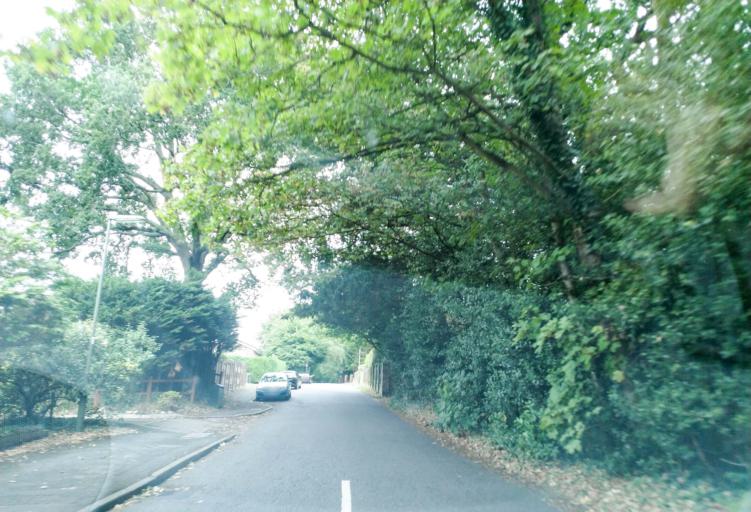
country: GB
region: England
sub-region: Surrey
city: Frimley
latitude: 51.3045
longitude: -0.7216
